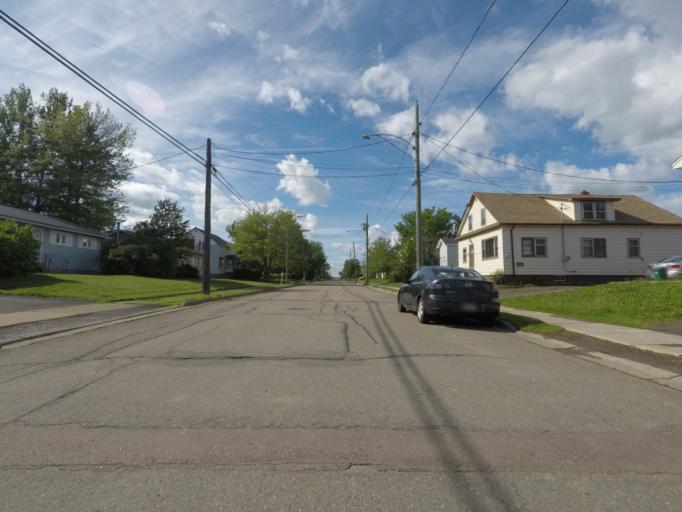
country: CA
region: New Brunswick
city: Moncton
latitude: 46.0991
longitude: -64.8204
